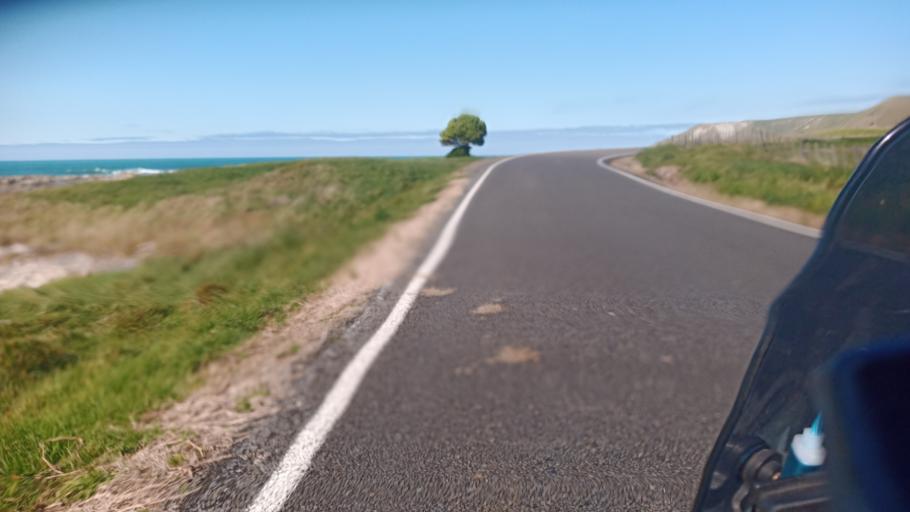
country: NZ
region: Gisborne
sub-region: Gisborne District
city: Gisborne
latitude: -39.0898
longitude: 177.9609
